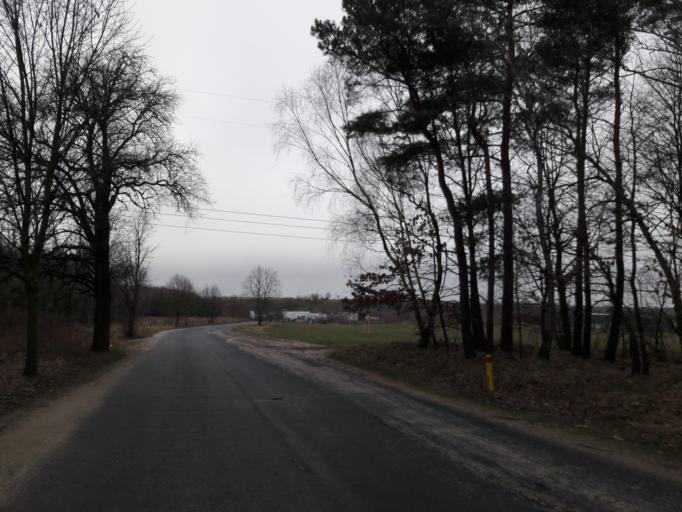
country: PL
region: Greater Poland Voivodeship
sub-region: Powiat poznanski
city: Suchy Las
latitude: 52.4911
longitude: 16.8882
